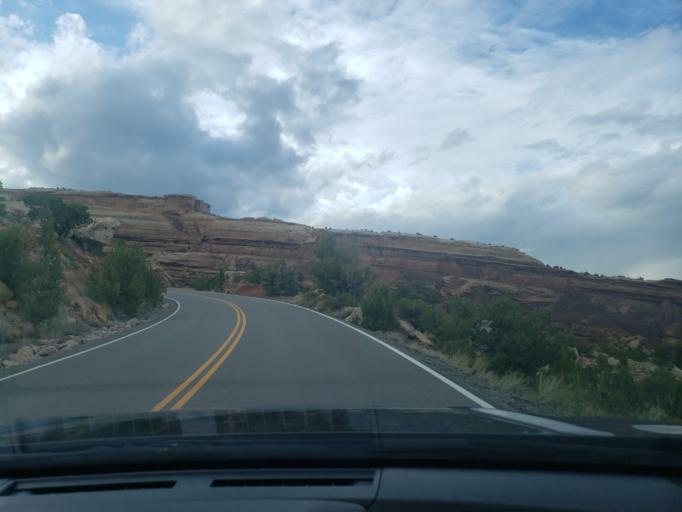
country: US
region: Colorado
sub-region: Mesa County
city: Redlands
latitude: 39.0276
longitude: -108.6413
